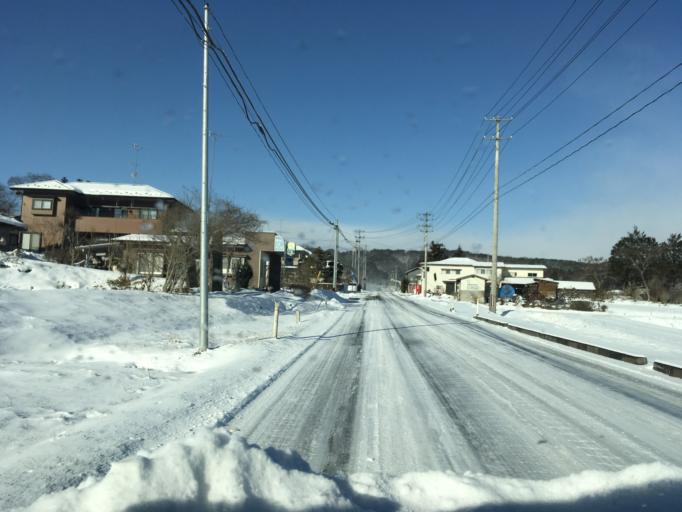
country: JP
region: Iwate
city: Ichinoseki
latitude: 38.8359
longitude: 141.2421
